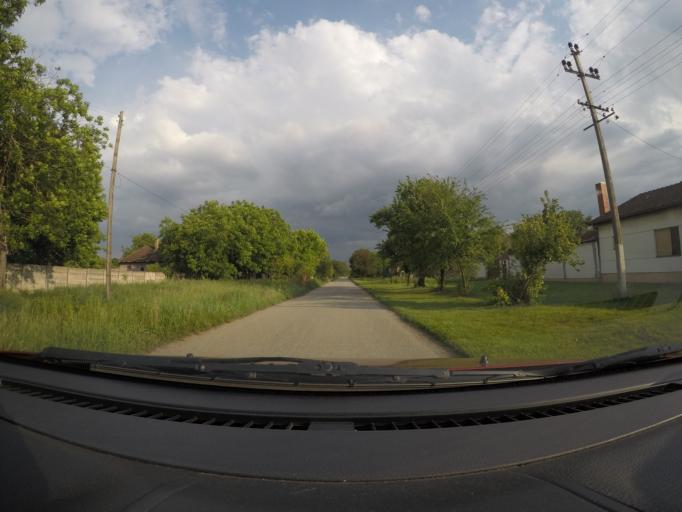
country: RS
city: Debeljaca
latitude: 45.0660
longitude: 20.6002
